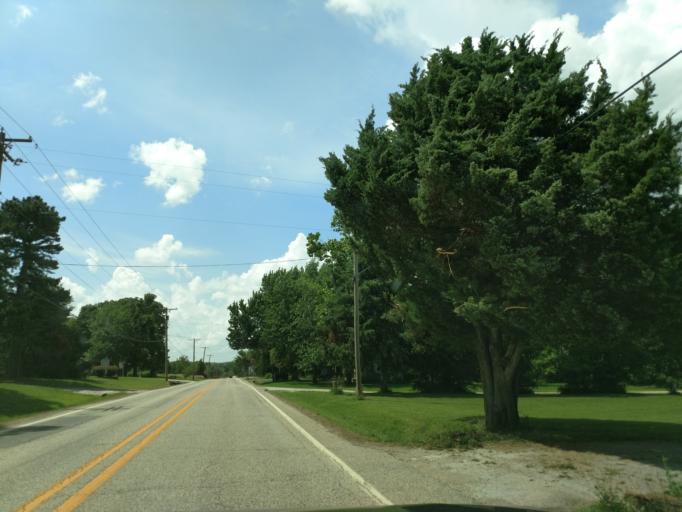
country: US
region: Arkansas
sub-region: Boone County
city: Harrison
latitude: 36.2551
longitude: -93.2236
